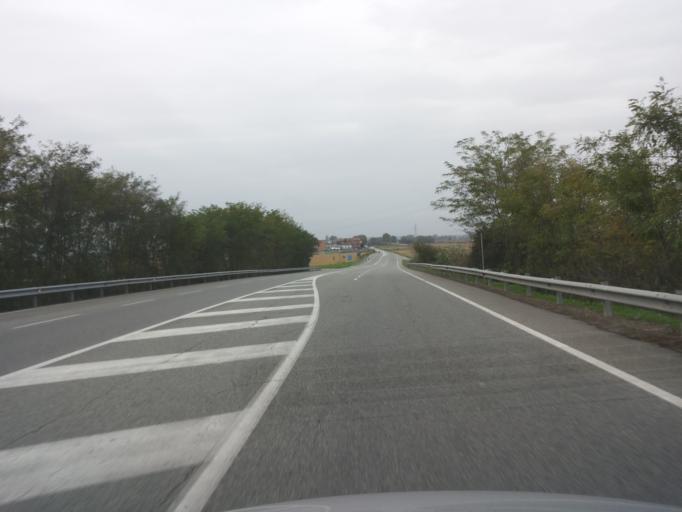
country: IT
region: Piedmont
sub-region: Provincia di Alessandria
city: Pontestura
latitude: 45.1772
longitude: 8.3321
